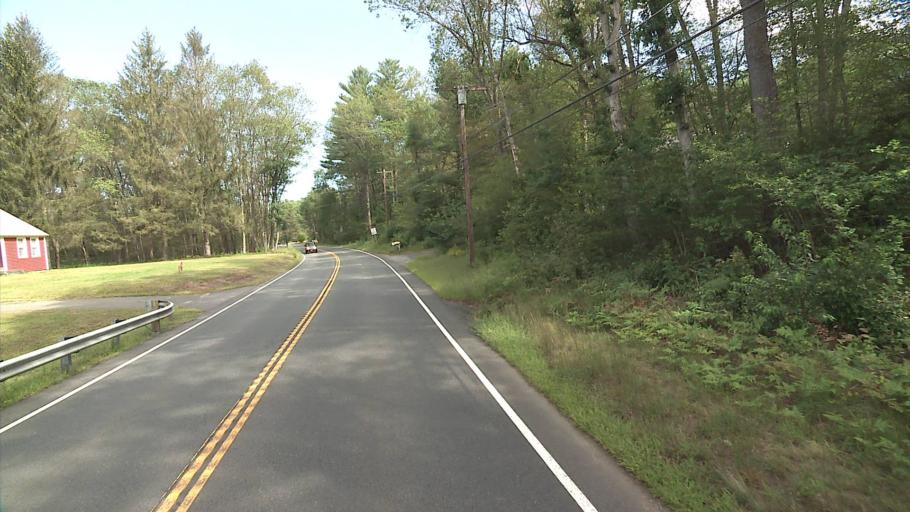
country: US
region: Connecticut
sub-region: Tolland County
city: Stafford
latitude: 42.0032
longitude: -72.3183
